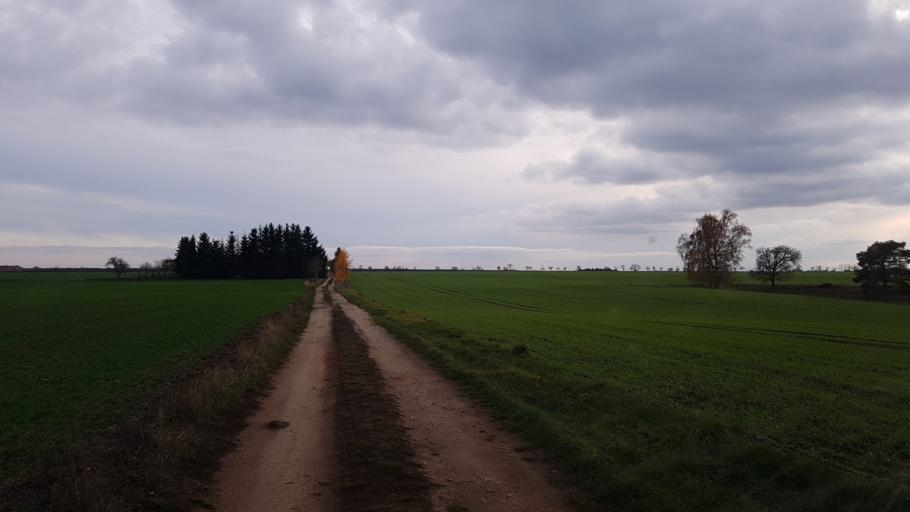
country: DE
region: Brandenburg
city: Schlieben
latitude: 51.6678
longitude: 13.4192
